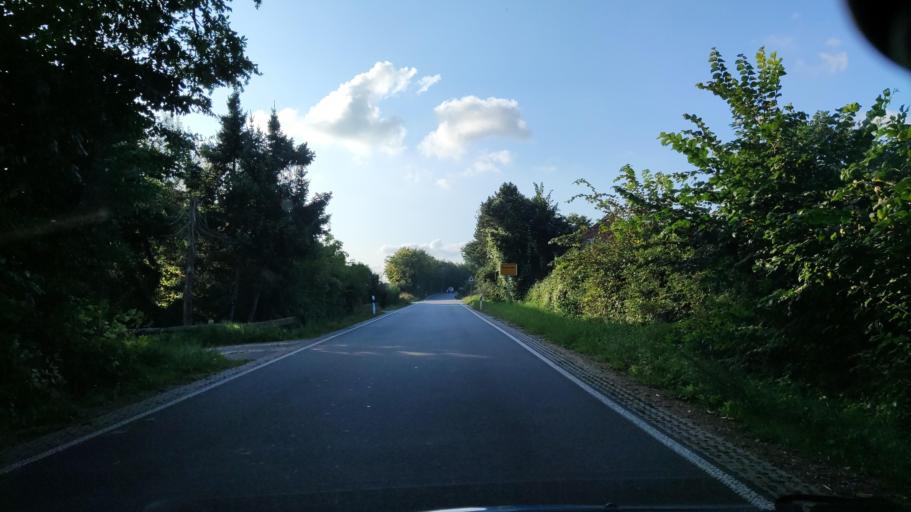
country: DE
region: Schleswig-Holstein
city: Bosdorf
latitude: 54.0975
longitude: 10.4849
